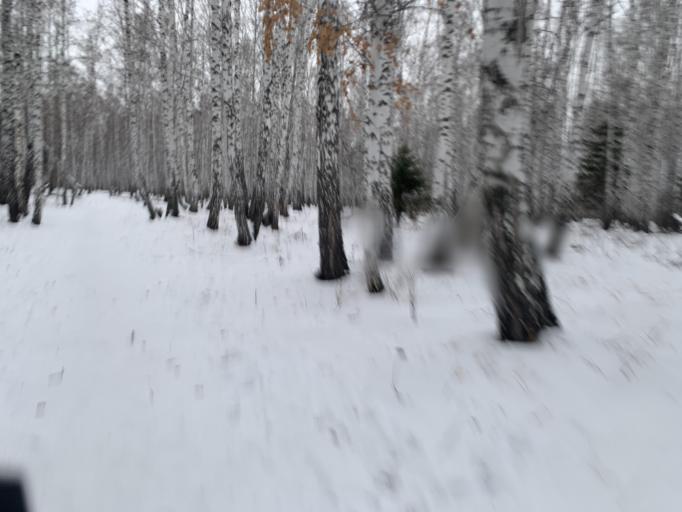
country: RU
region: Chelyabinsk
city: Roshchino
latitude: 55.2038
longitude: 61.2600
